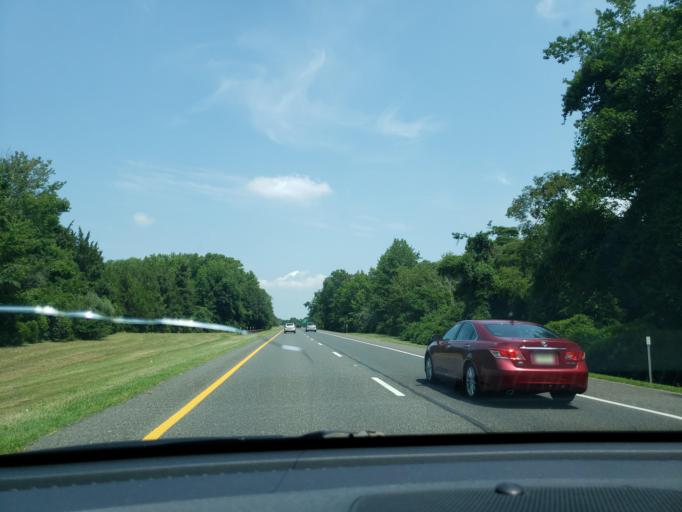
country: US
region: New Jersey
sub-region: Cape May County
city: Erma
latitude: 38.9773
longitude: -74.8905
